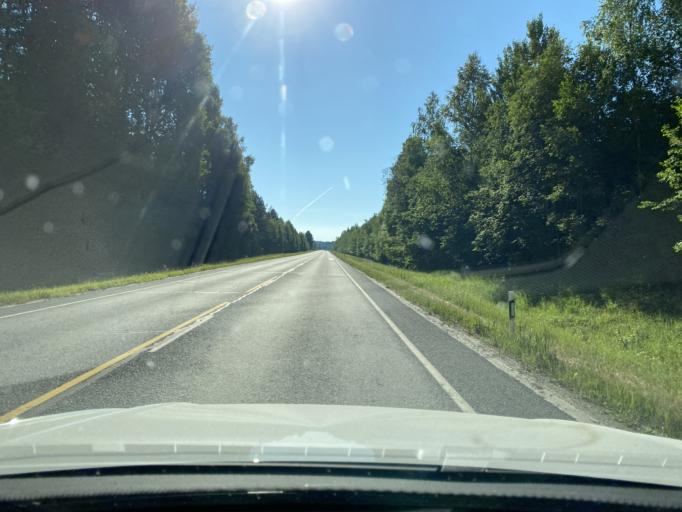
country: FI
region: Haeme
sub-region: Forssa
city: Tammela
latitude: 60.8266
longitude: 23.9385
